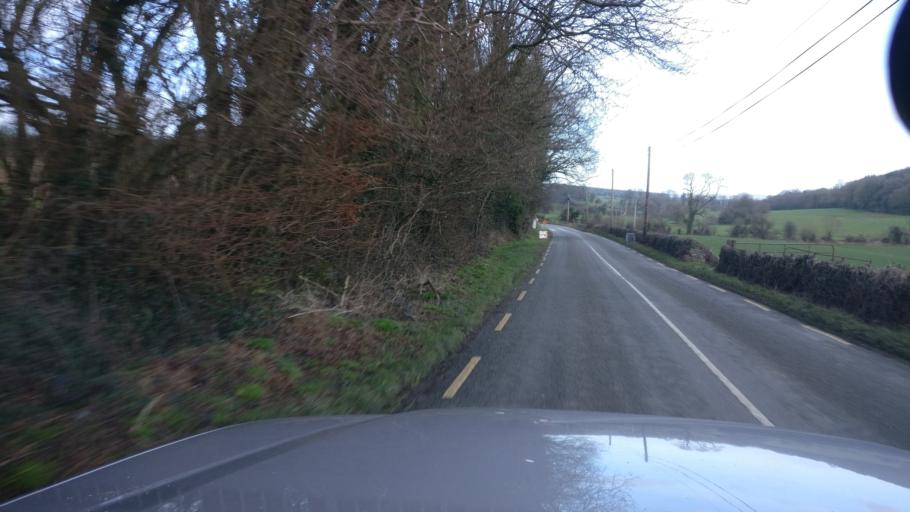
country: IE
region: Leinster
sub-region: Kilkenny
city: Castlecomer
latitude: 52.8169
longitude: -7.2134
